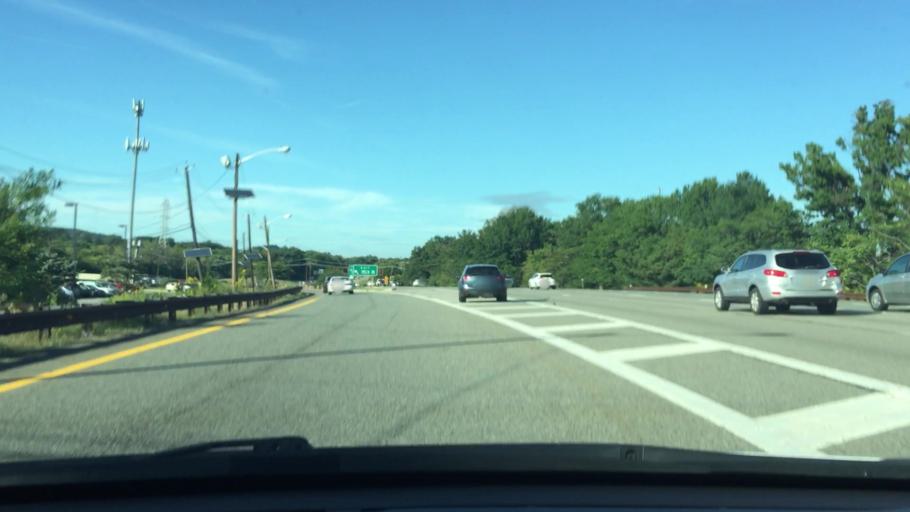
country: US
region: New Jersey
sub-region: Passaic County
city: Clifton
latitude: 40.8539
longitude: -74.1745
